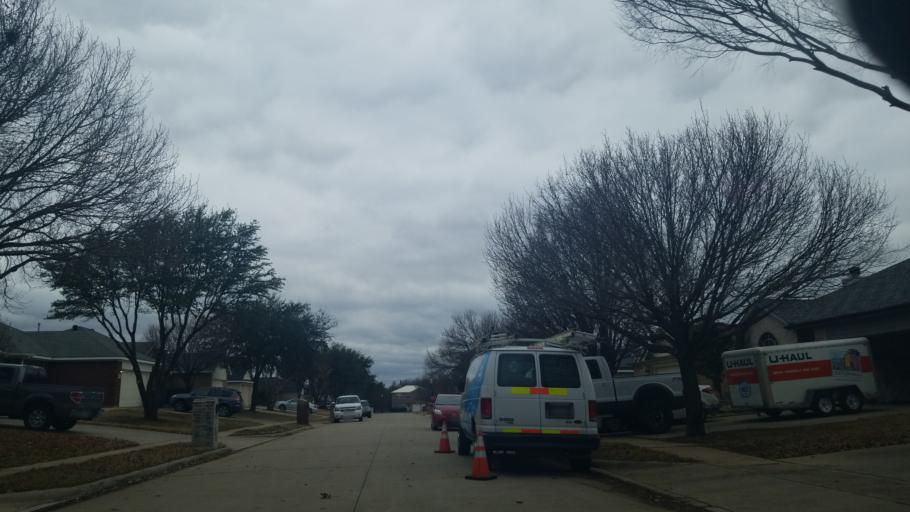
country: US
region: Texas
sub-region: Denton County
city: Corinth
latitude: 33.1326
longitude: -97.0869
